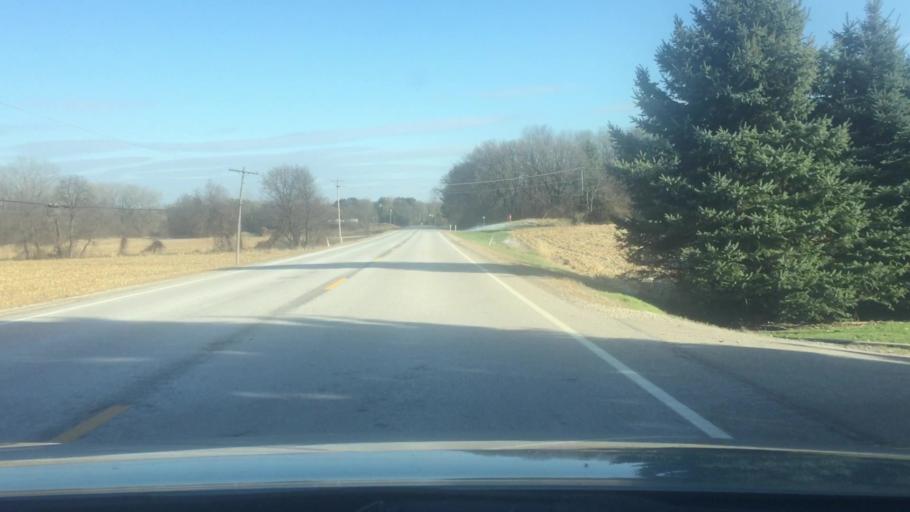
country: US
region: Wisconsin
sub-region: Jefferson County
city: Lake Koshkonong
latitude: 42.9481
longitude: -88.8965
